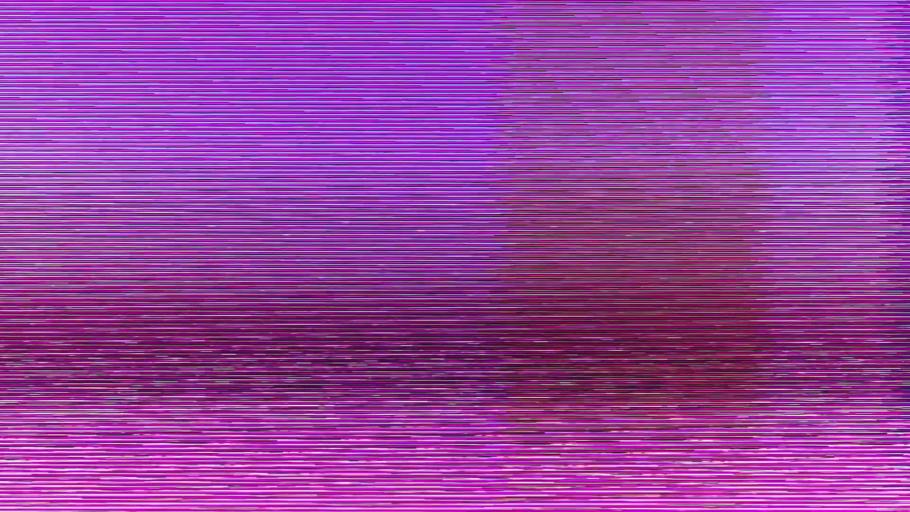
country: US
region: Michigan
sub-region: Oakland County
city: Farmington Hills
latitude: 42.4765
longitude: -83.3574
